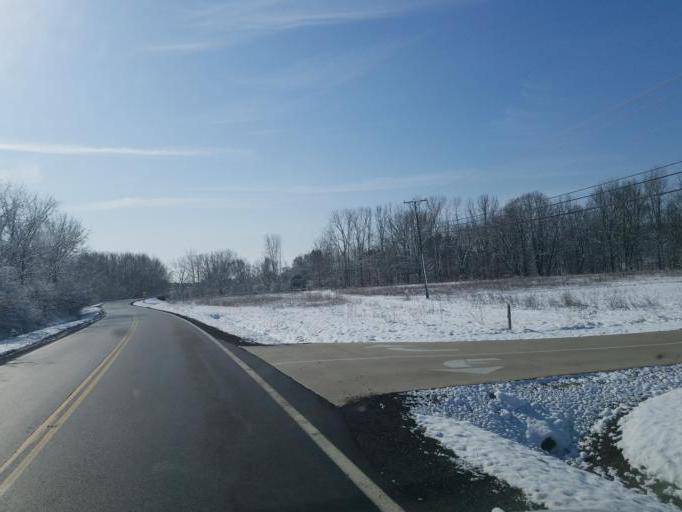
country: US
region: Ohio
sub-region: Sandusky County
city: Bellville
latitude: 40.6261
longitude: -82.5319
